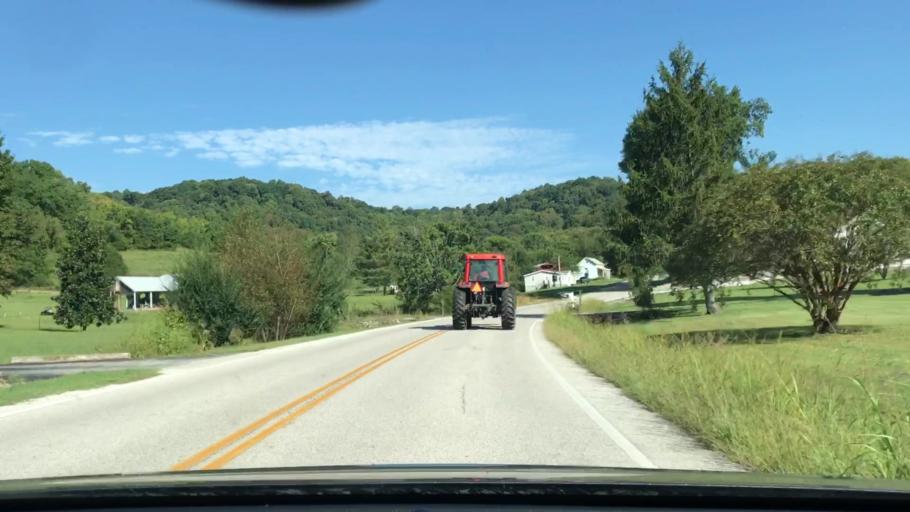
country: US
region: Tennessee
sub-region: Smith County
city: Carthage
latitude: 36.2893
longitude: -85.9512
